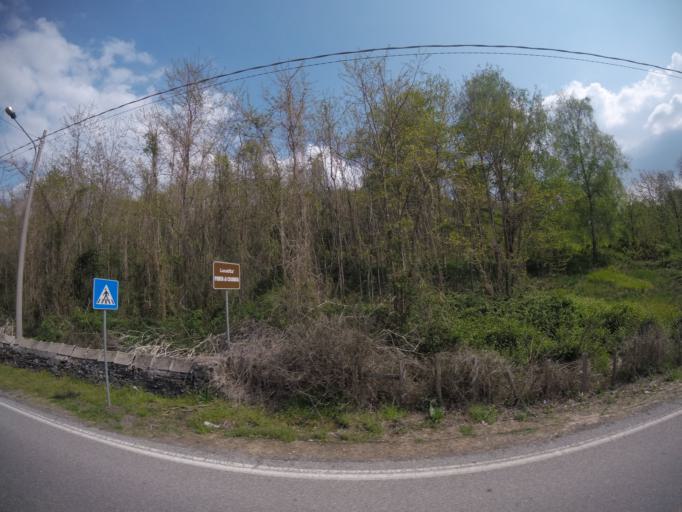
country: IT
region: Piedmont
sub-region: Provincia di Novara
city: Pettenasco
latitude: 45.8267
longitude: 8.3994
